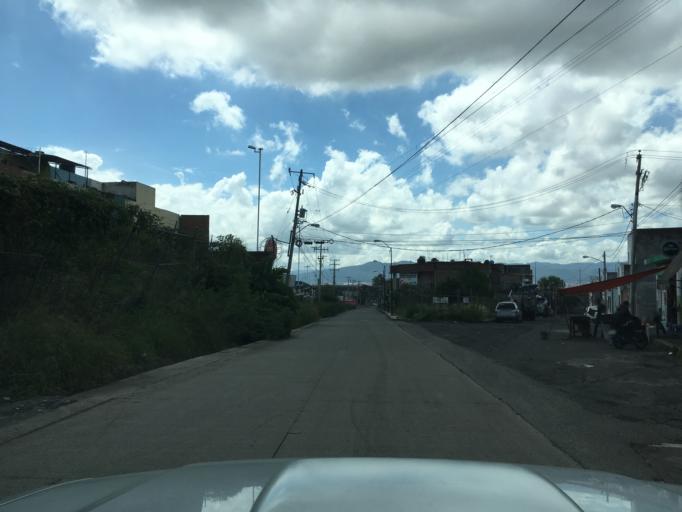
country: MX
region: Michoacan
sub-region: Tarimbaro
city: Fraccionamiento Metropolis II
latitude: 19.7253
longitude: -101.2272
